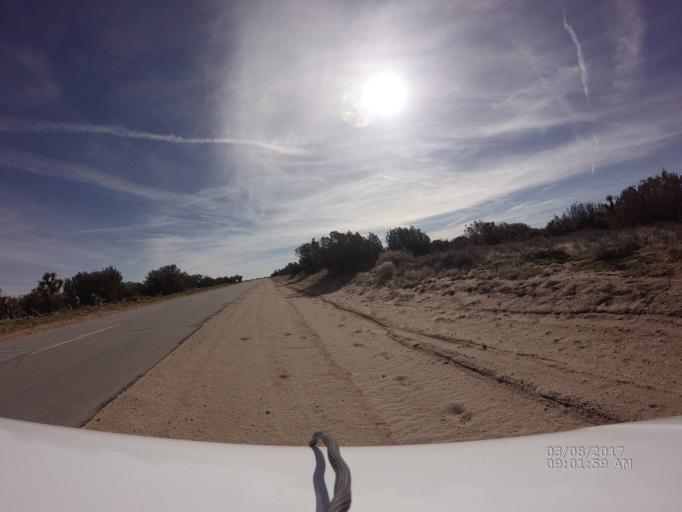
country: US
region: California
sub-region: Los Angeles County
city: Green Valley
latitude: 34.7603
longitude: -118.5083
